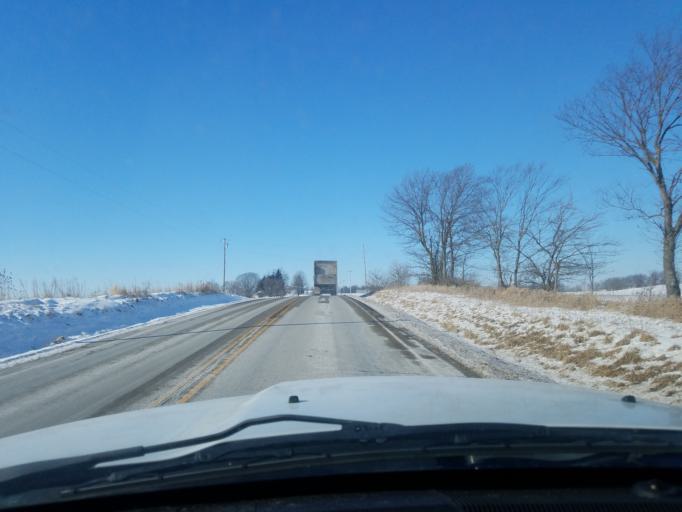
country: US
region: Indiana
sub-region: Noble County
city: Avilla
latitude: 41.3947
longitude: -85.2778
